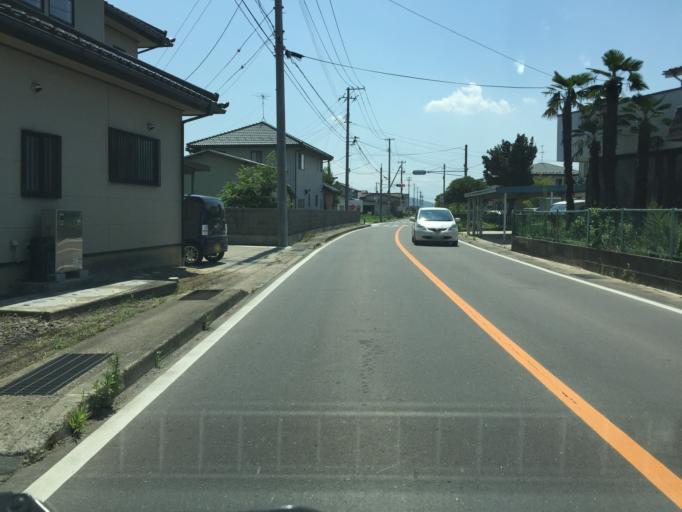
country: JP
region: Fukushima
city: Hobaramachi
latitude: 37.8350
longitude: 140.5720
